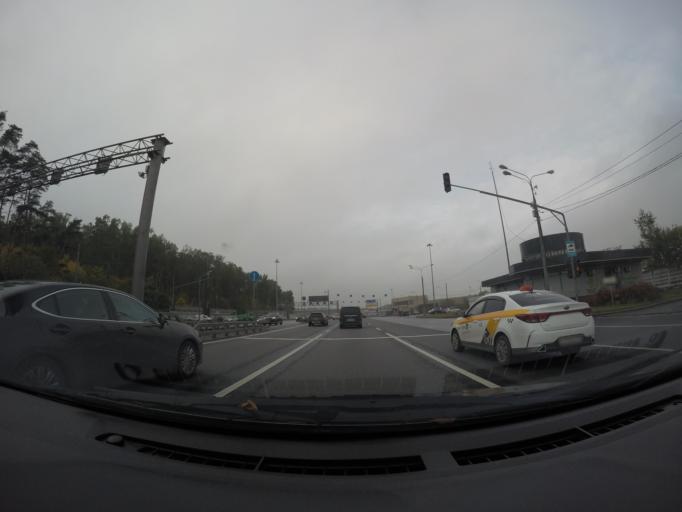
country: RU
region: Moscow
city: Rublevo
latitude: 55.7884
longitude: 37.3800
